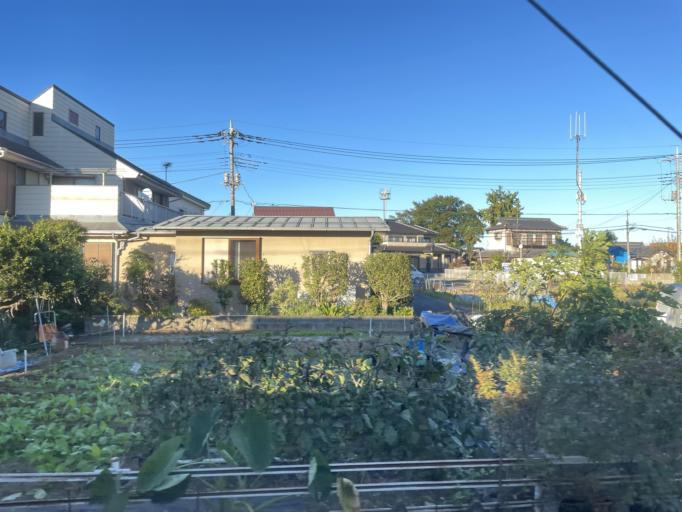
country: JP
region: Saitama
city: Sugito
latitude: 36.0271
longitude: 139.7228
